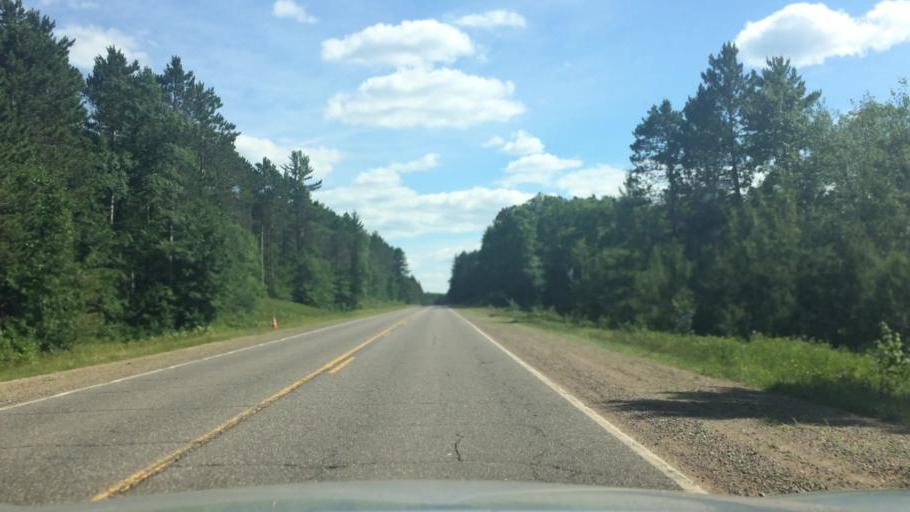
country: US
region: Wisconsin
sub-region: Vilas County
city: Lac du Flambeau
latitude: 46.0571
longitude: -89.6496
